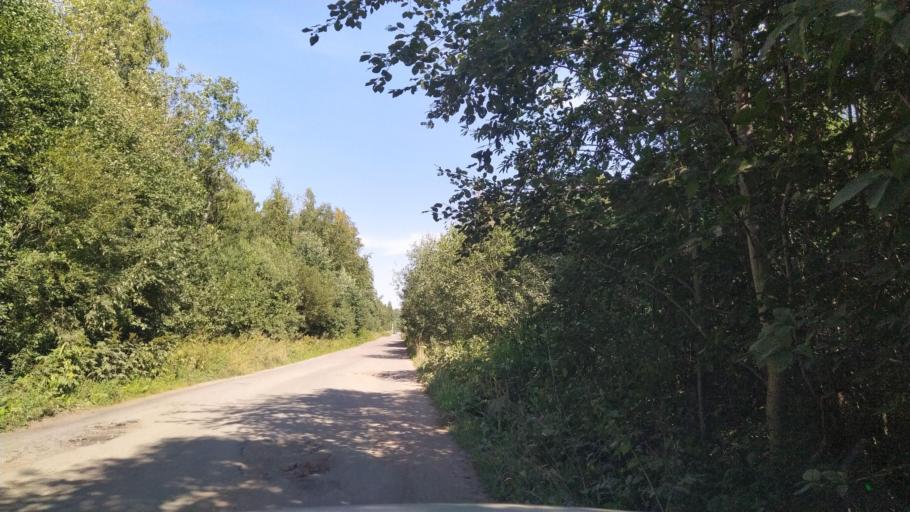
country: RU
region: Leningrad
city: Siverskiy
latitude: 59.2844
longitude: 30.0297
